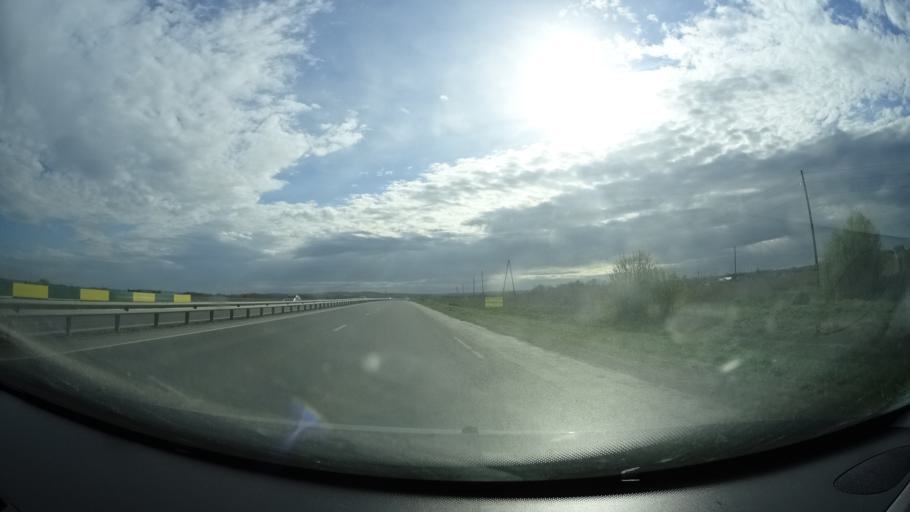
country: RU
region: Perm
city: Kultayevo
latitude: 57.8895
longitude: 55.9453
